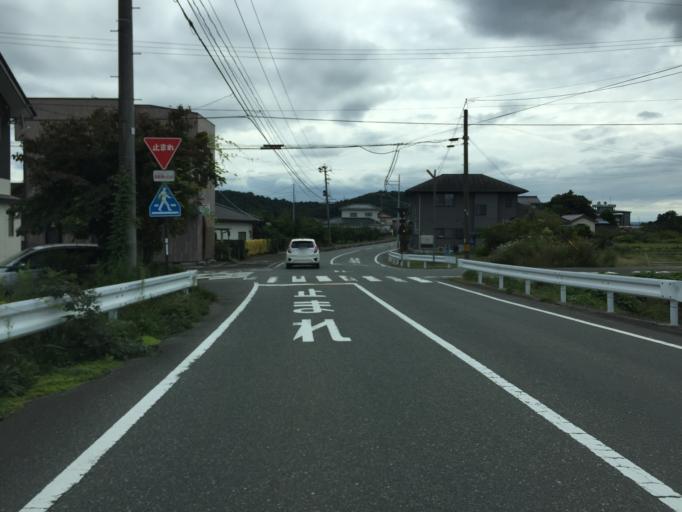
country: JP
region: Fukushima
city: Hobaramachi
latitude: 37.8195
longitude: 140.5125
